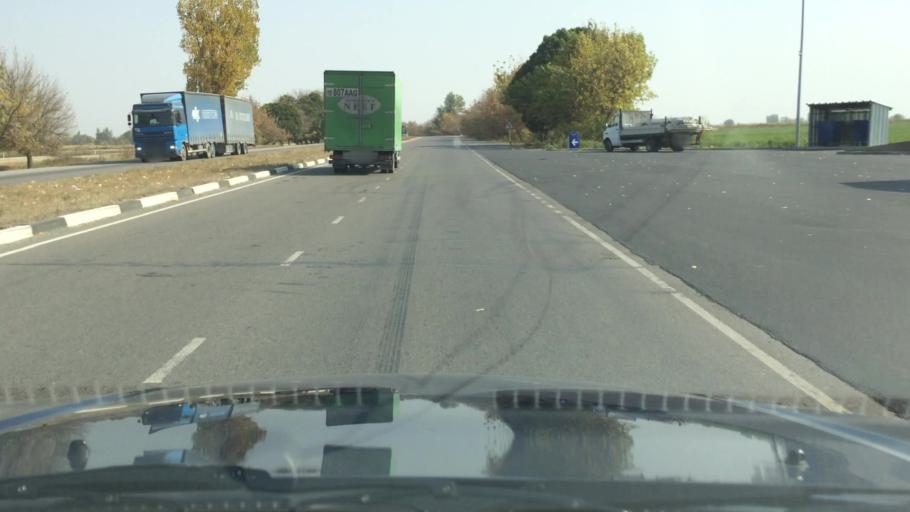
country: KG
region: Chuy
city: Lebedinovka
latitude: 42.9228
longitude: 74.7546
